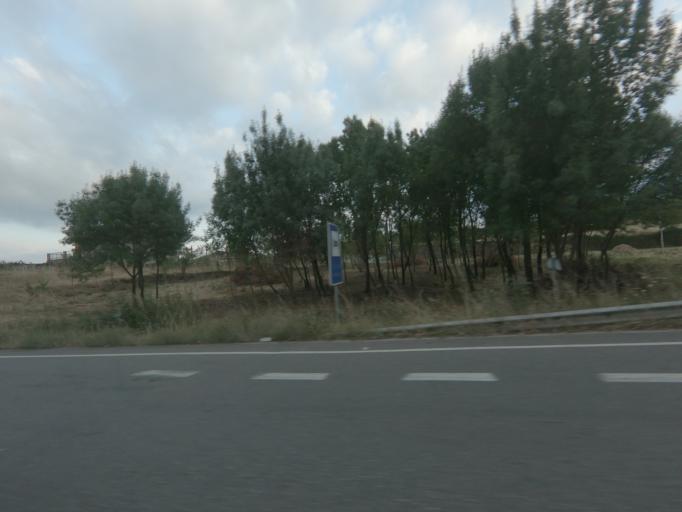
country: ES
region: Galicia
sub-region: Provincia de Ourense
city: Taboadela
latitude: 42.2848
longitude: -7.8436
